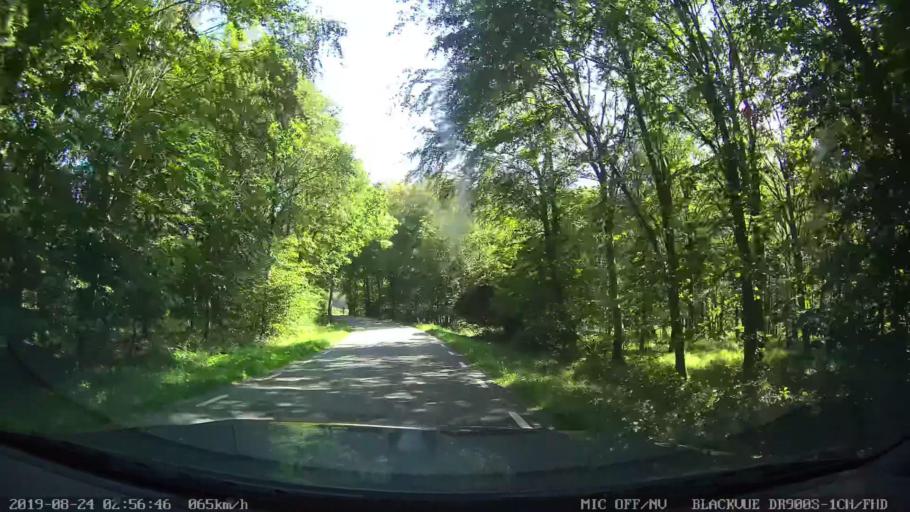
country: SE
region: Skane
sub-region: Trelleborgs Kommun
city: Anderslov
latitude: 55.4873
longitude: 13.3985
